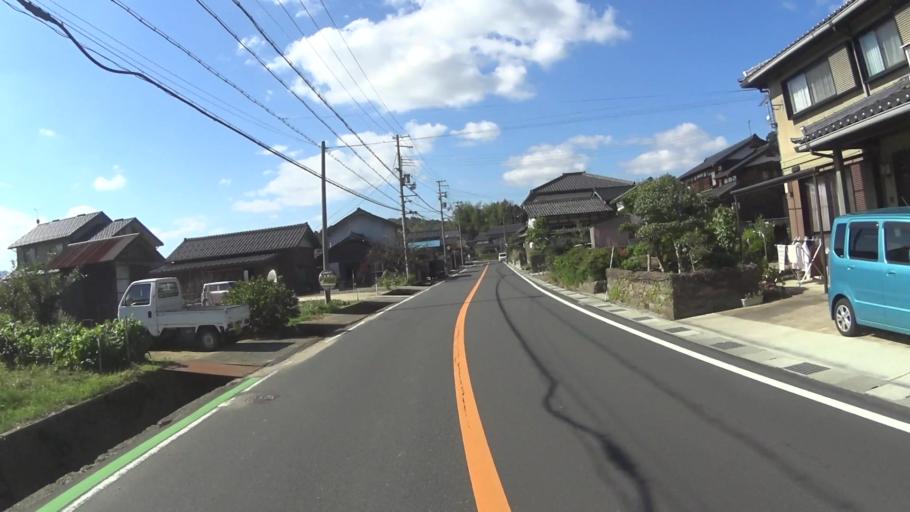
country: JP
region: Kyoto
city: Miyazu
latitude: 35.6337
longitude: 135.0766
